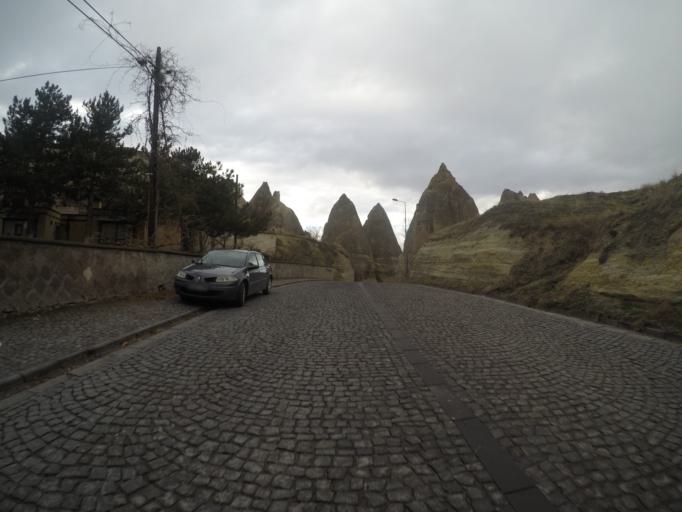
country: TR
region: Nevsehir
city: Goereme
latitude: 38.6435
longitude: 34.8356
